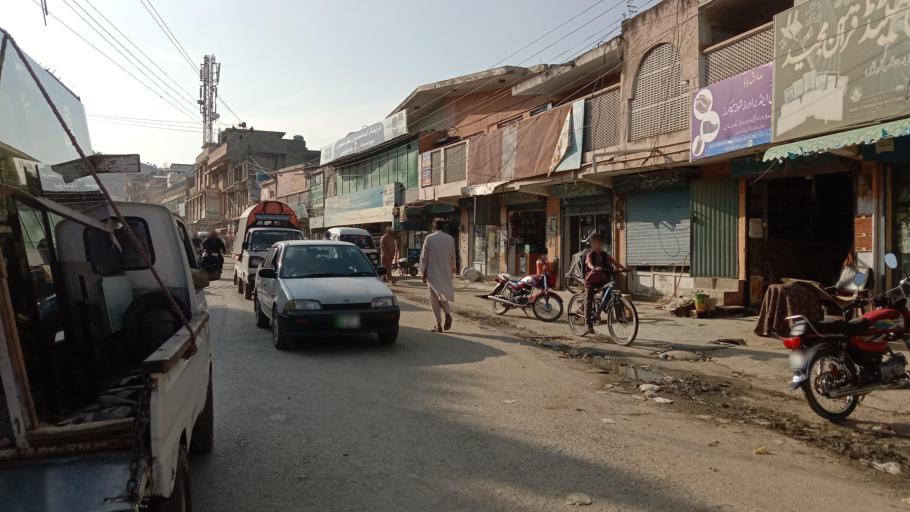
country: PK
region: Khyber Pakhtunkhwa
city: Abbottabad
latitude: 34.1977
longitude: 73.2317
